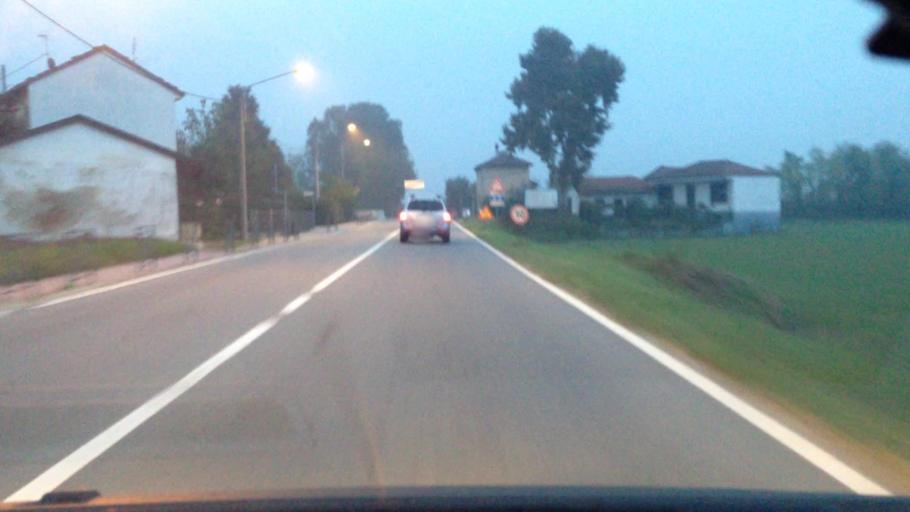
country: IT
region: Piedmont
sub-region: Provincia di Asti
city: Rocca d'Arazzo
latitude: 44.9066
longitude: 8.2846
